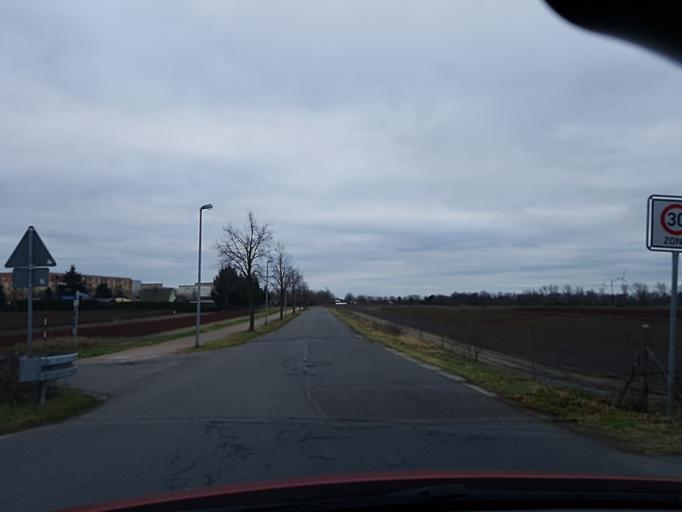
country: DE
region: Brandenburg
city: Elsterwerda
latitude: 51.4654
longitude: 13.4995
